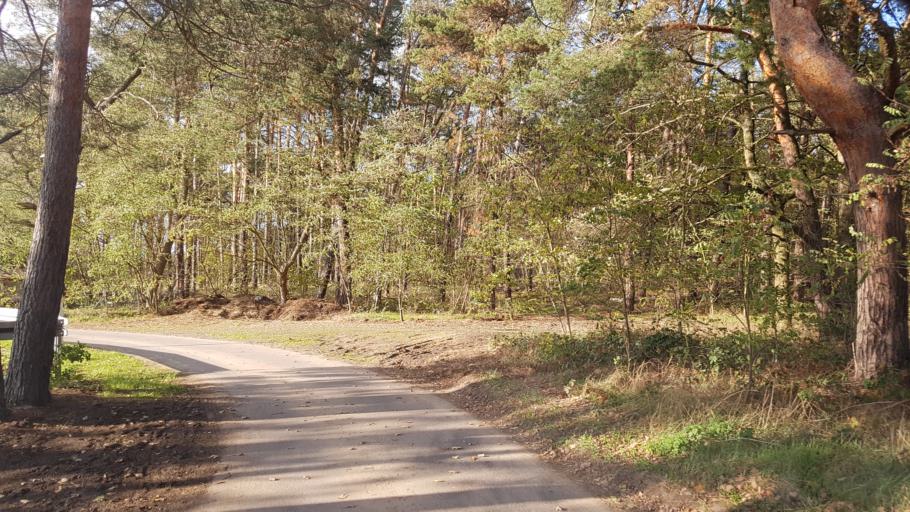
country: DE
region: Brandenburg
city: Schonewalde
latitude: 51.7011
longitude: 13.5766
